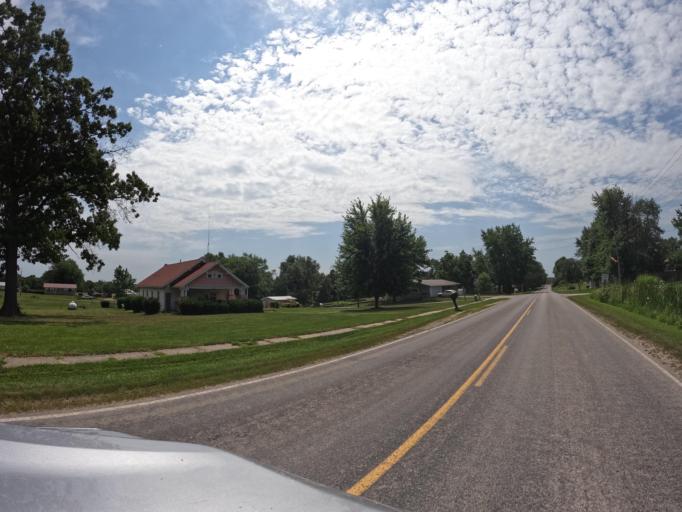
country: US
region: Iowa
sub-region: Appanoose County
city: Centerville
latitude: 40.7847
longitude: -92.9448
